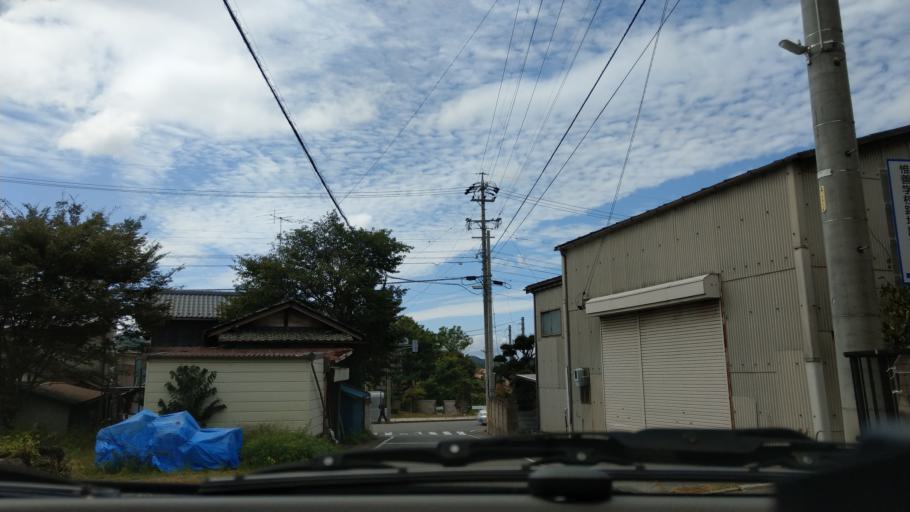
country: JP
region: Nagano
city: Komoro
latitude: 36.3216
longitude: 138.4334
